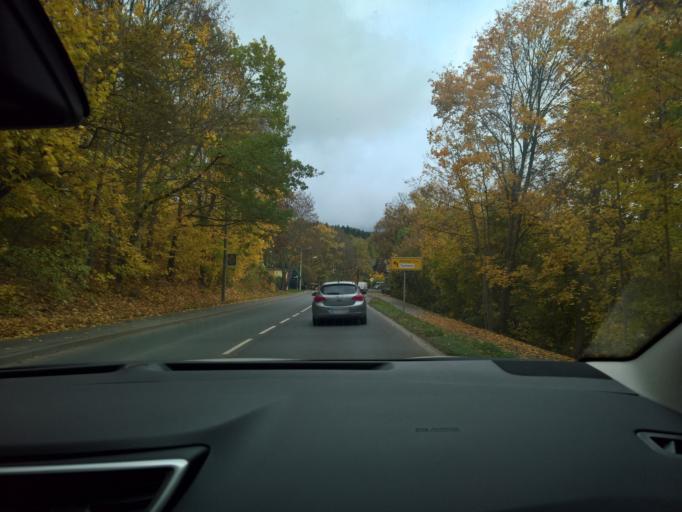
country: DE
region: Saxony
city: Plauen
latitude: 50.4783
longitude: 12.1437
